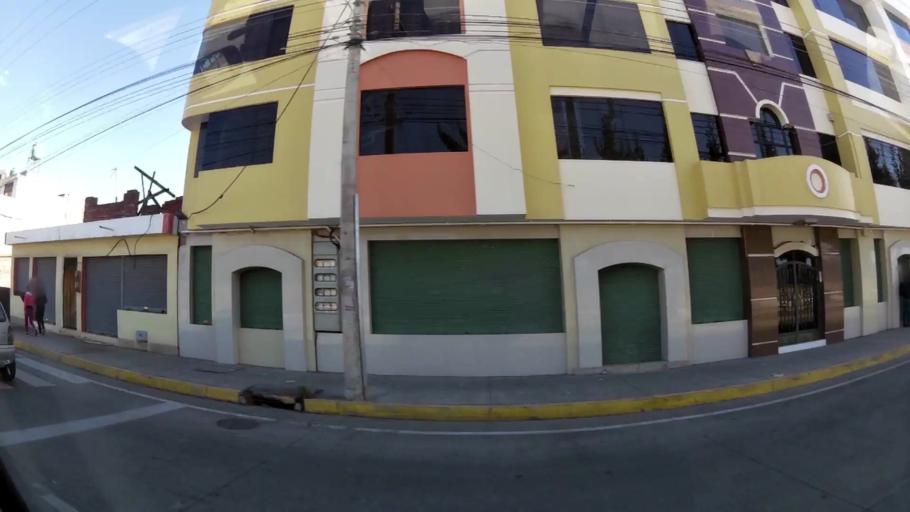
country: EC
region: Chimborazo
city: Riobamba
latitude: -1.6683
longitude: -78.6671
